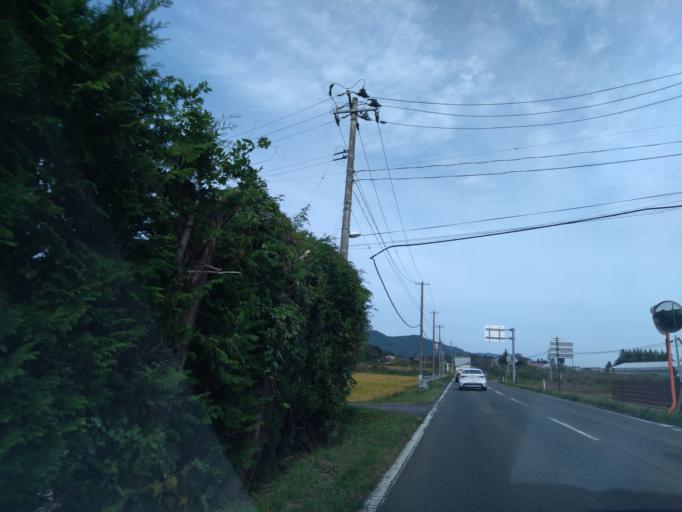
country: JP
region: Iwate
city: Hanamaki
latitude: 39.4271
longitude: 141.0844
